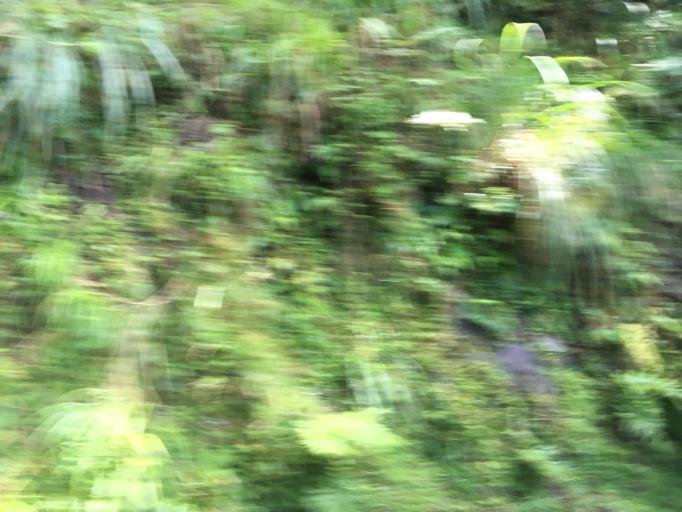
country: TW
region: Taiwan
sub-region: Yilan
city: Yilan
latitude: 24.6202
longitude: 121.4809
